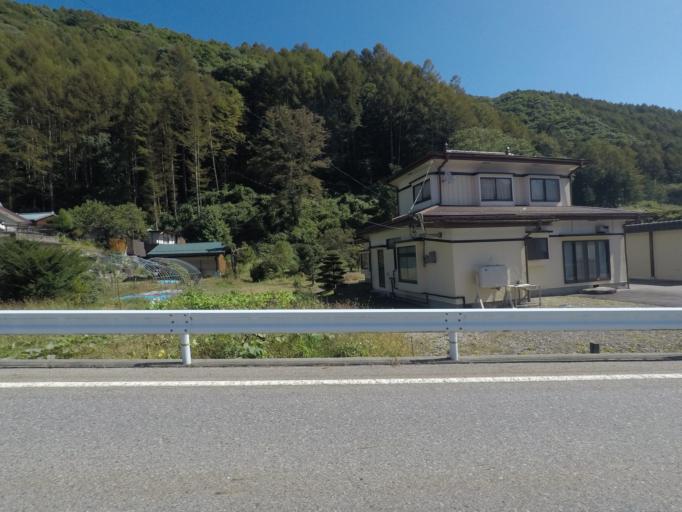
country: JP
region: Nagano
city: Shiojiri
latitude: 35.9855
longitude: 137.7424
